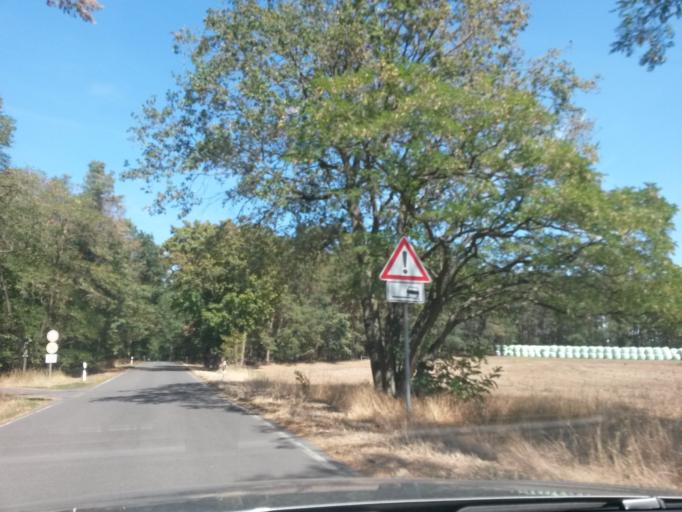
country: DE
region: Saxony-Anhalt
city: Pretzsch
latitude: 51.7489
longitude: 12.8431
